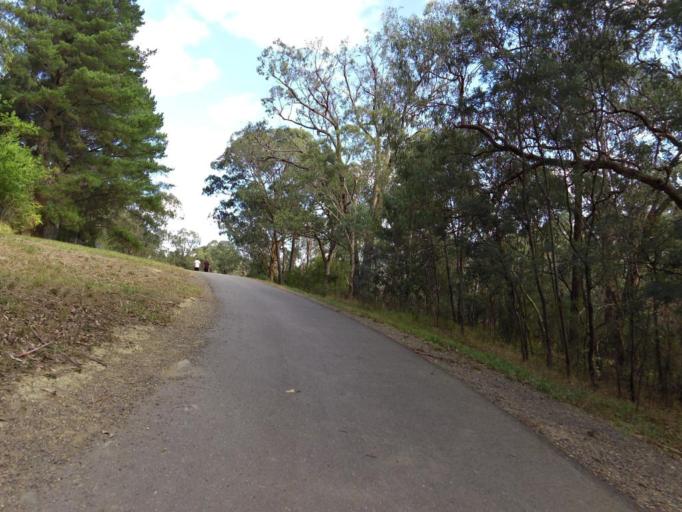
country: AU
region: Victoria
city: Mitcham
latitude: -37.7991
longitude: 145.2032
